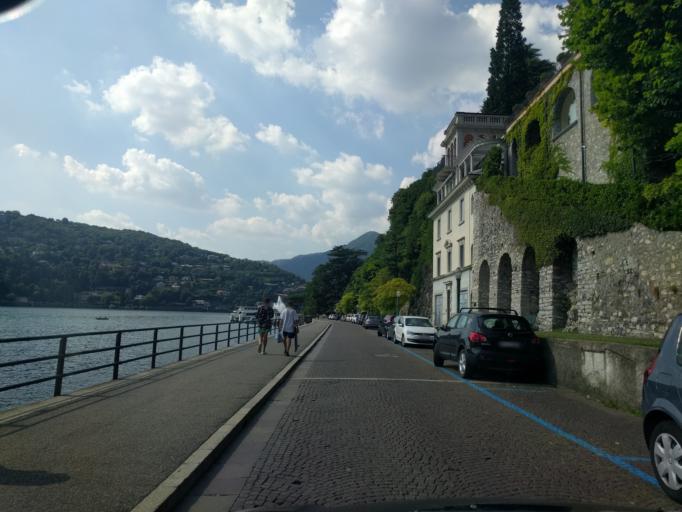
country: IT
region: Lombardy
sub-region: Provincia di Como
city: Brunate
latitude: 45.8209
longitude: 9.0797
